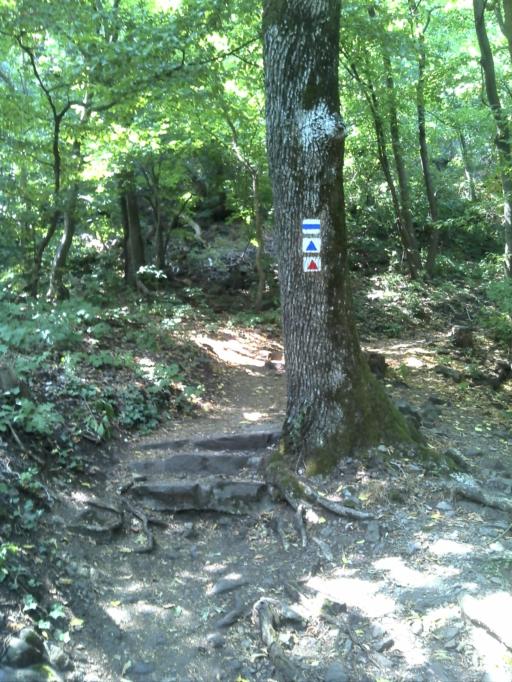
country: HU
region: Veszprem
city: Badacsonytomaj
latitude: 46.7988
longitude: 17.4985
